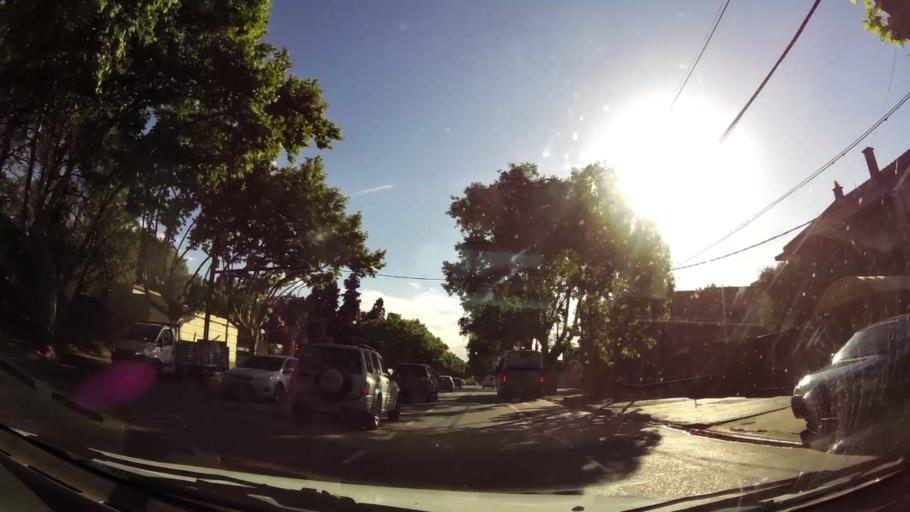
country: AR
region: Buenos Aires
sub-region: Partido de San Isidro
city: San Isidro
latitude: -34.4792
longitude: -58.5221
